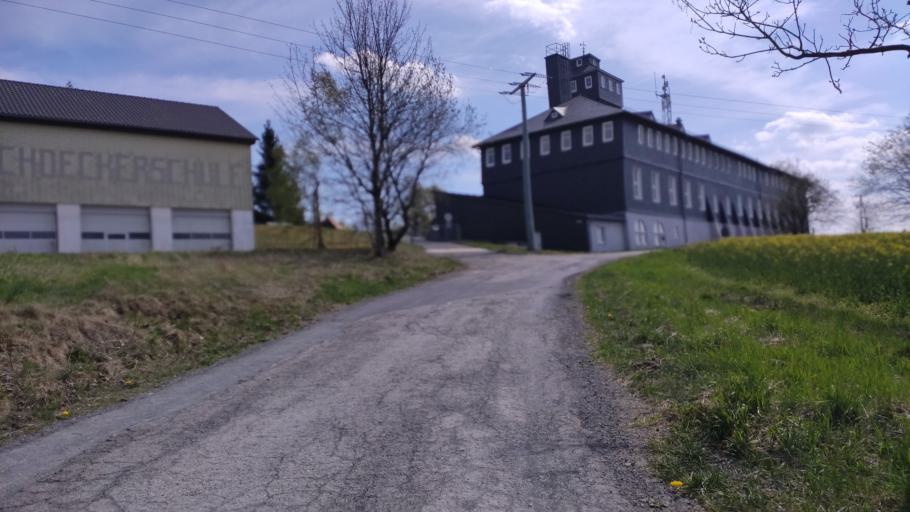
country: DE
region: Bavaria
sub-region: Upper Franconia
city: Ludwigsstadt
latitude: 50.4807
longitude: 11.4485
